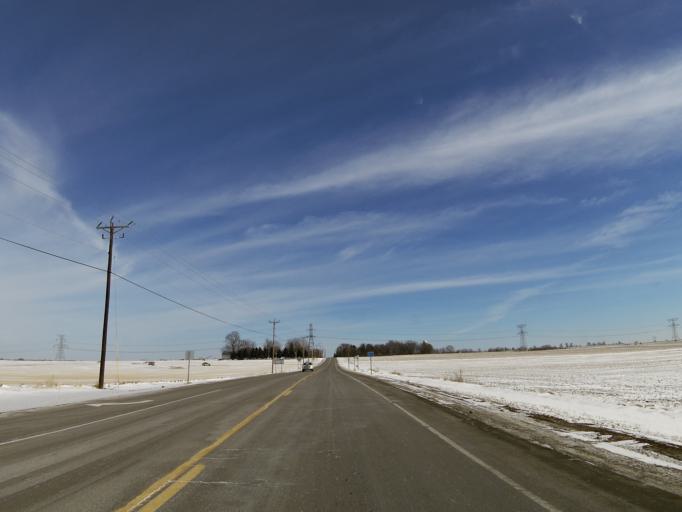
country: US
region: Minnesota
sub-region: Washington County
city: Afton
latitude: 44.8911
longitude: -92.8620
